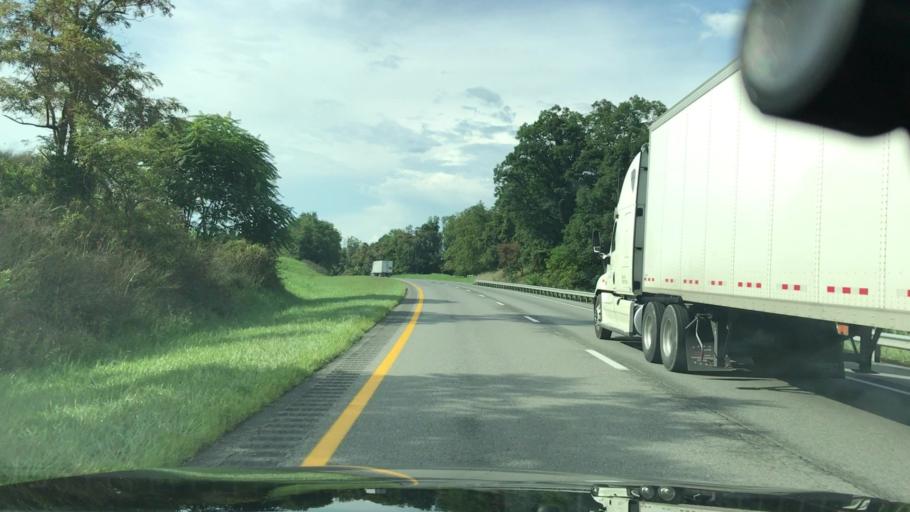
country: US
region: Virginia
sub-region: Pulaski County
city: Pulaski
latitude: 36.8992
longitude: -80.8753
